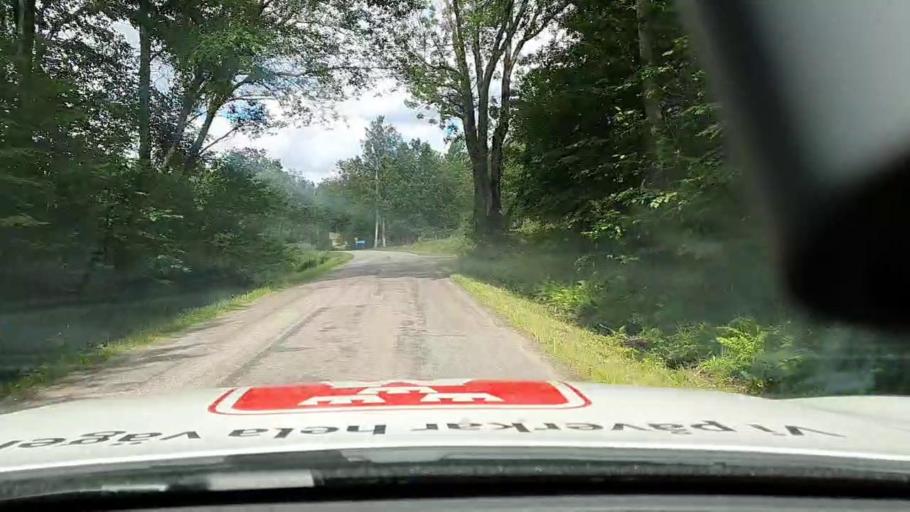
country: SE
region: Vaestra Goetaland
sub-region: Karlsborgs Kommun
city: Molltorp
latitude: 58.5800
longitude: 14.2691
